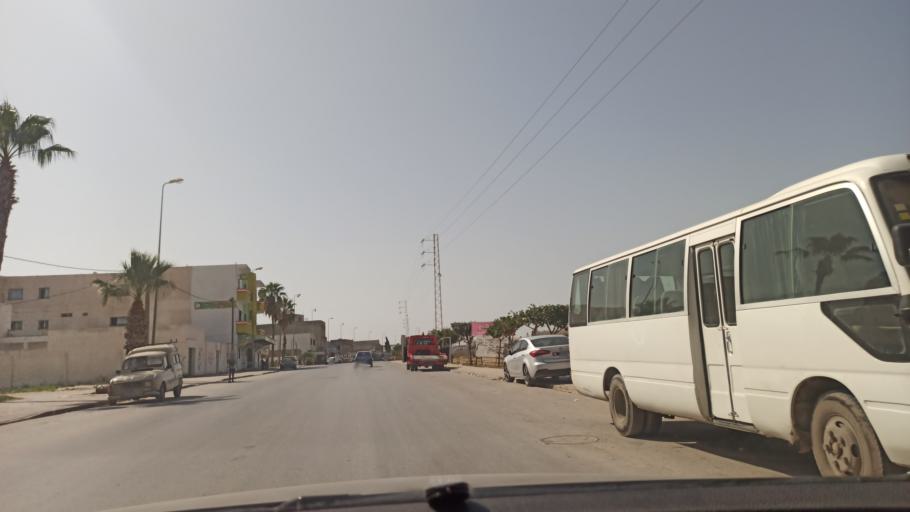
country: TN
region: Manouba
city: Manouba
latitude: 36.7648
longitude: 10.1104
